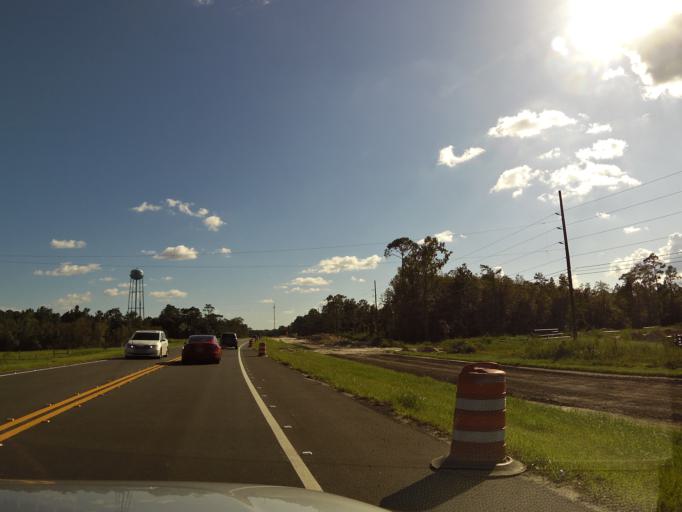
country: US
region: Florida
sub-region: Wakulla County
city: Crawfordville
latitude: 30.2779
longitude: -84.3555
